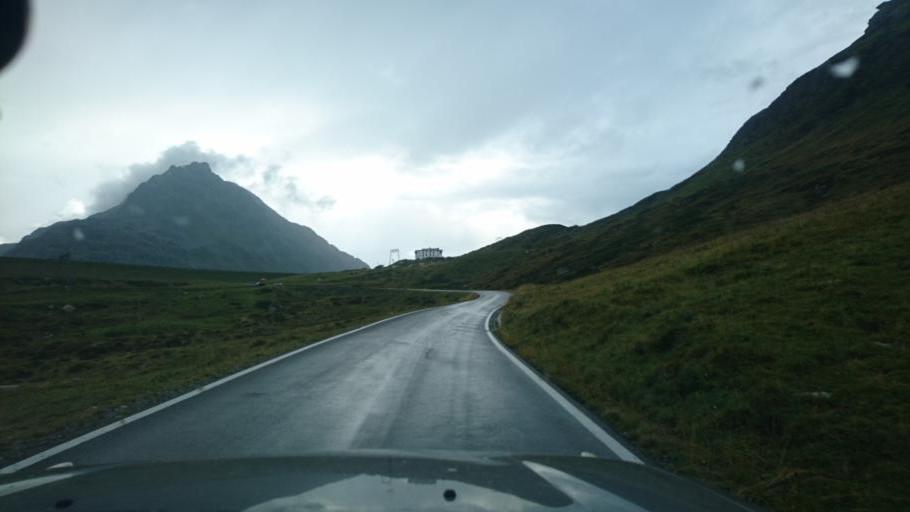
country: AT
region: Tyrol
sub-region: Politischer Bezirk Landeck
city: Galtur
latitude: 46.9197
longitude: 10.1029
